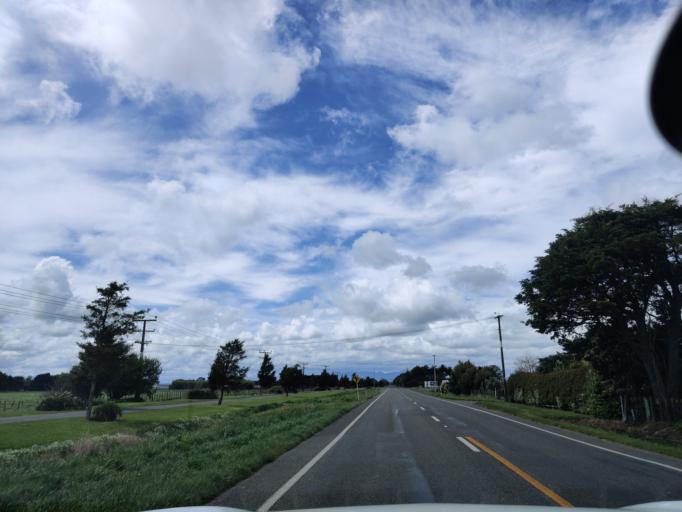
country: NZ
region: Manawatu-Wanganui
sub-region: Palmerston North City
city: Palmerston North
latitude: -40.3767
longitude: 175.5654
